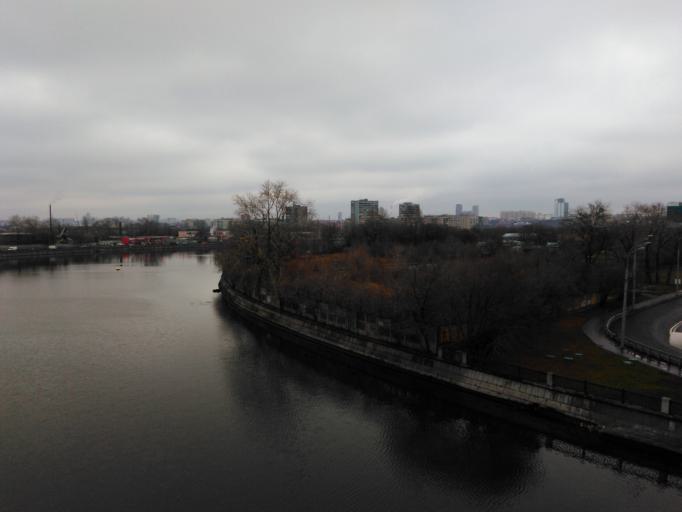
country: RU
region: Moscow
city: Zamoskvorech'ye
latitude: 55.7055
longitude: 37.6288
